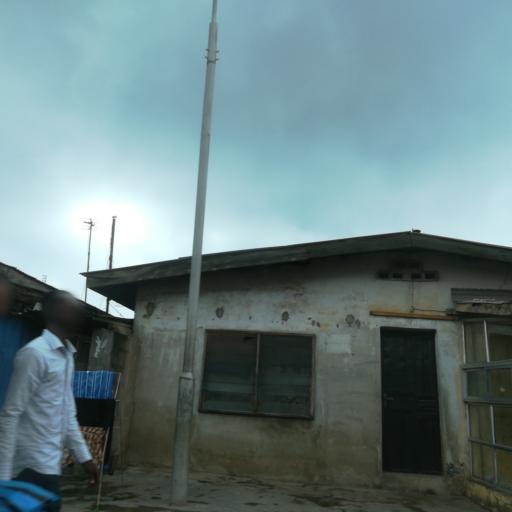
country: NG
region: Lagos
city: Agege
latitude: 6.5965
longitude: 3.2998
